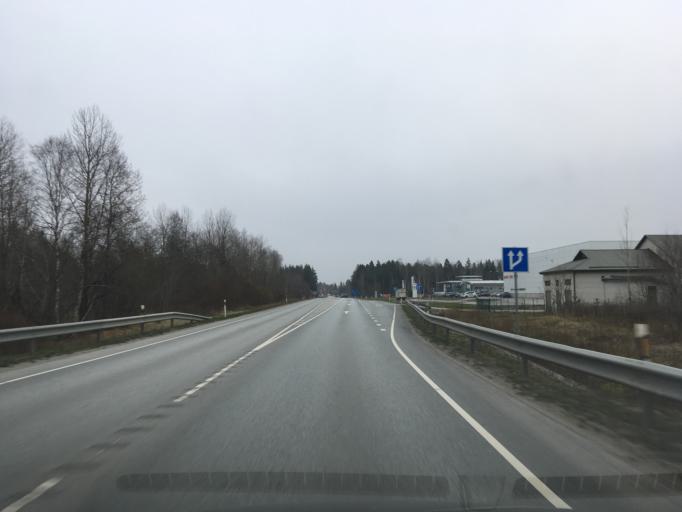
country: EE
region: Ida-Virumaa
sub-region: Johvi vald
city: Johvi
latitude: 59.3644
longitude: 27.4486
